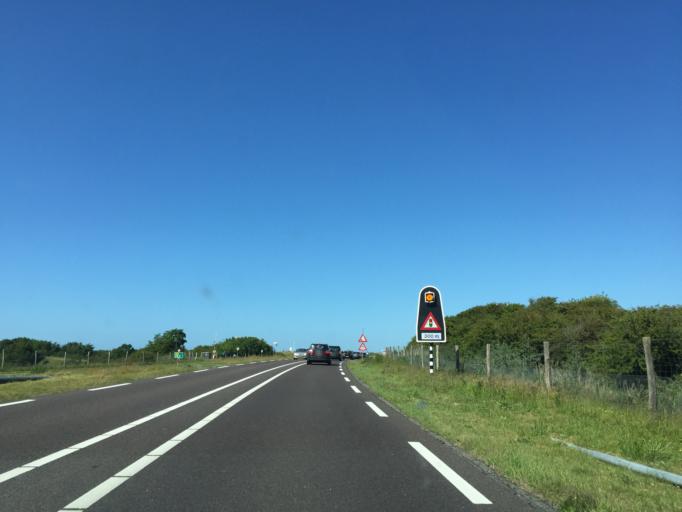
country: NL
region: Zeeland
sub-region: Gemeente Veere
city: Veere
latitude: 51.5824
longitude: 3.6245
